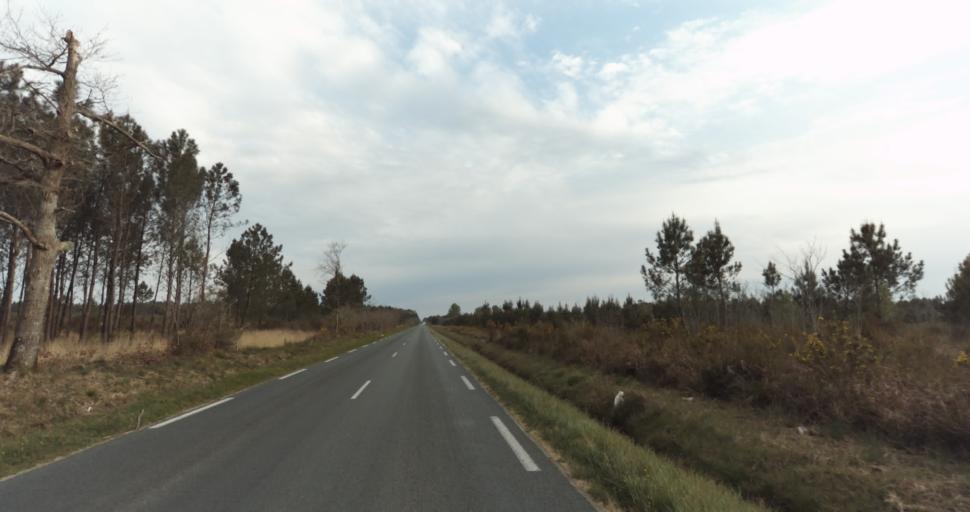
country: FR
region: Aquitaine
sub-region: Departement de la Gironde
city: Martignas-sur-Jalle
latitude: 44.7904
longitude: -0.7758
